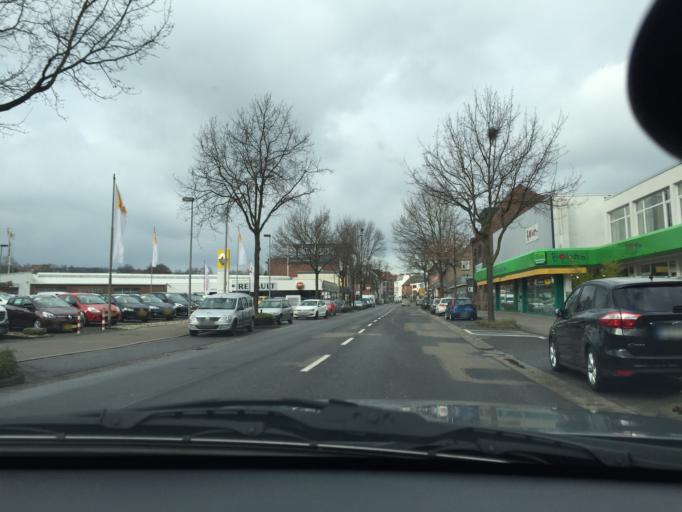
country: DE
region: North Rhine-Westphalia
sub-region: Regierungsbezirk Dusseldorf
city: Kleve
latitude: 51.7865
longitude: 6.1457
